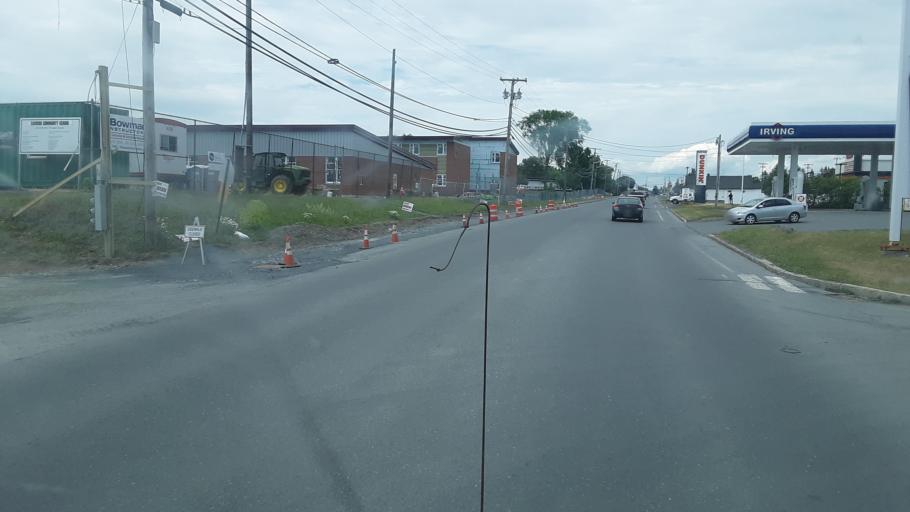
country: US
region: Maine
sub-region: Aroostook County
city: Caribou
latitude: 46.8625
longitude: -68.0048
